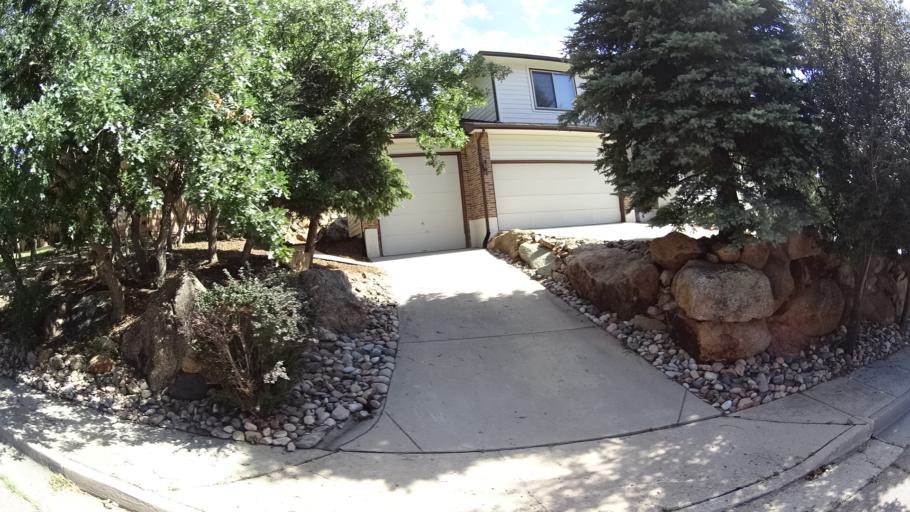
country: US
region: Colorado
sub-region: El Paso County
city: Fort Carson
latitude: 38.7545
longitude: -104.8339
